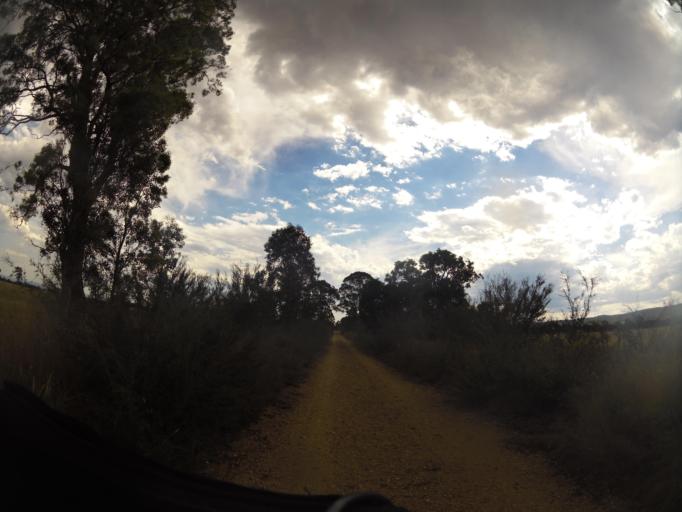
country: AU
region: Victoria
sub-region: Wellington
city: Heyfield
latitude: -38.0312
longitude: 146.6617
